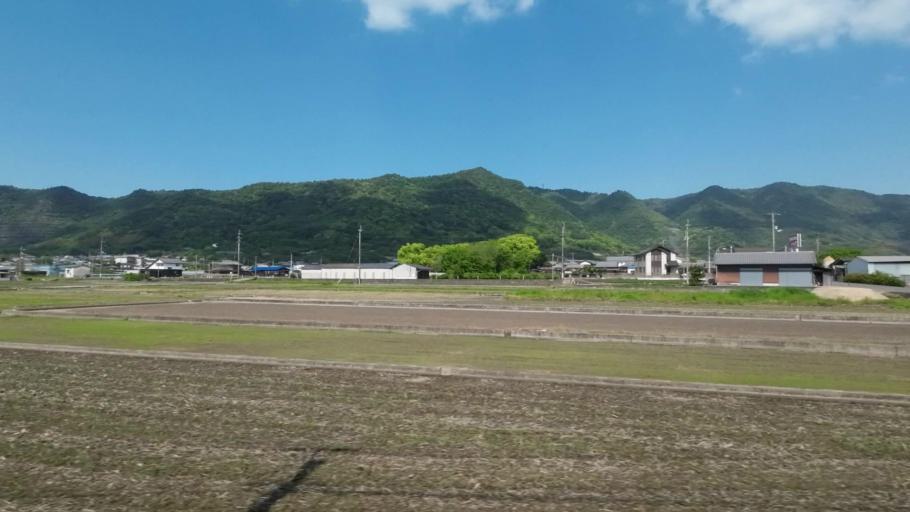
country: JP
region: Kagawa
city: Kan'onjicho
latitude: 34.1566
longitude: 133.6883
